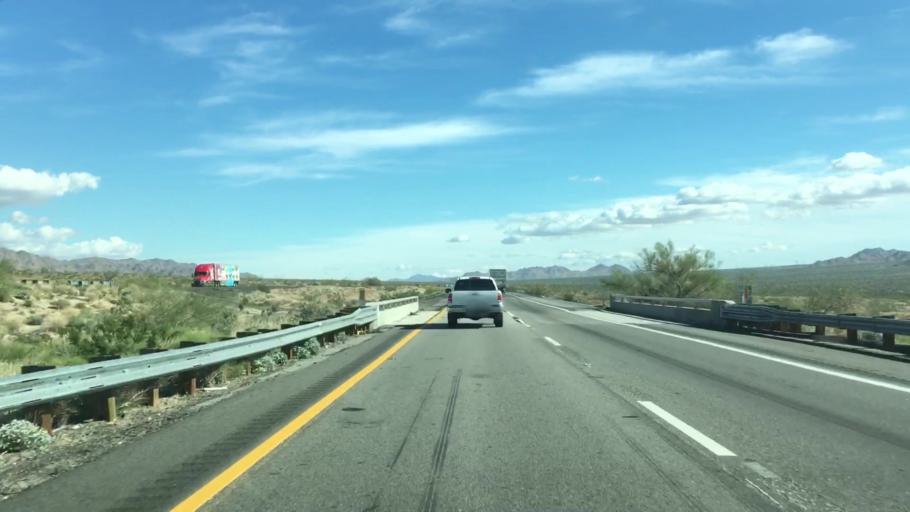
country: US
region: California
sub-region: Riverside County
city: Mecca
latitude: 33.6636
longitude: -115.8642
